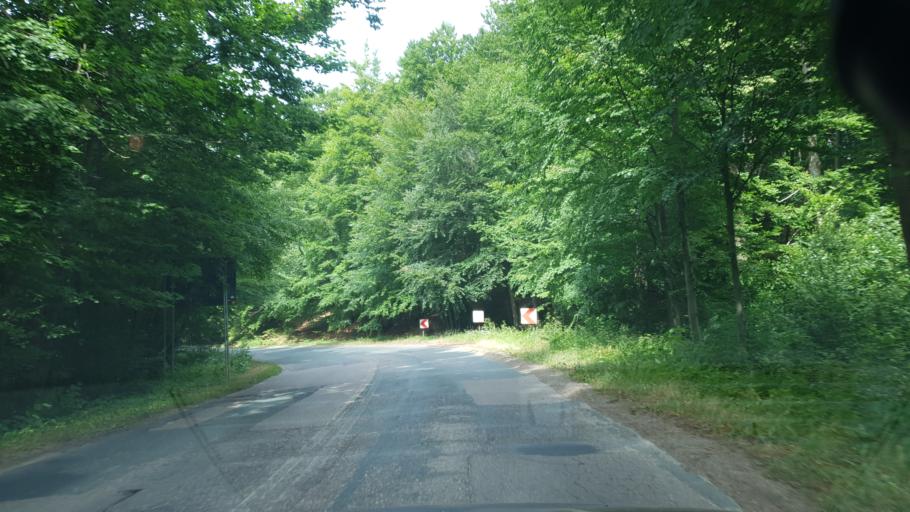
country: PL
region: Pomeranian Voivodeship
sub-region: Powiat kartuski
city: Chmielno
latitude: 54.2757
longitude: 18.0957
